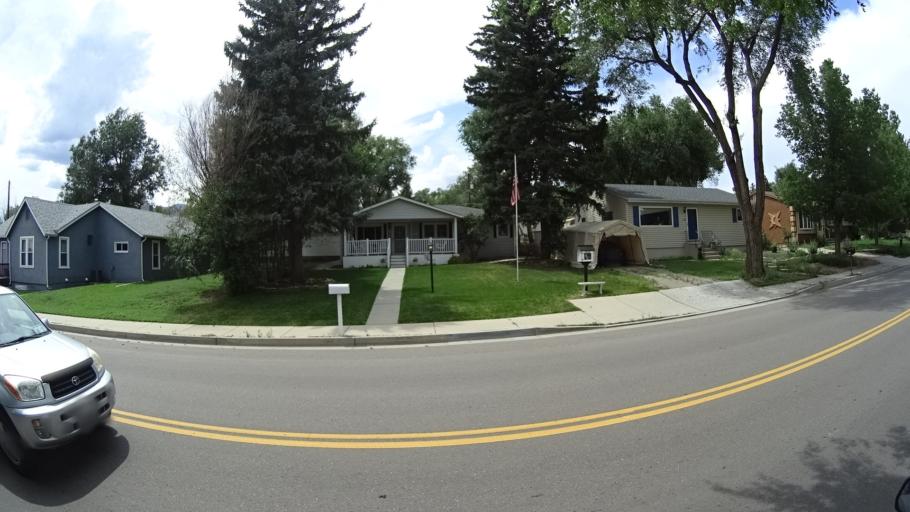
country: US
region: Colorado
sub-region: El Paso County
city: Colorado Springs
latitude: 38.8623
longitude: -104.8359
